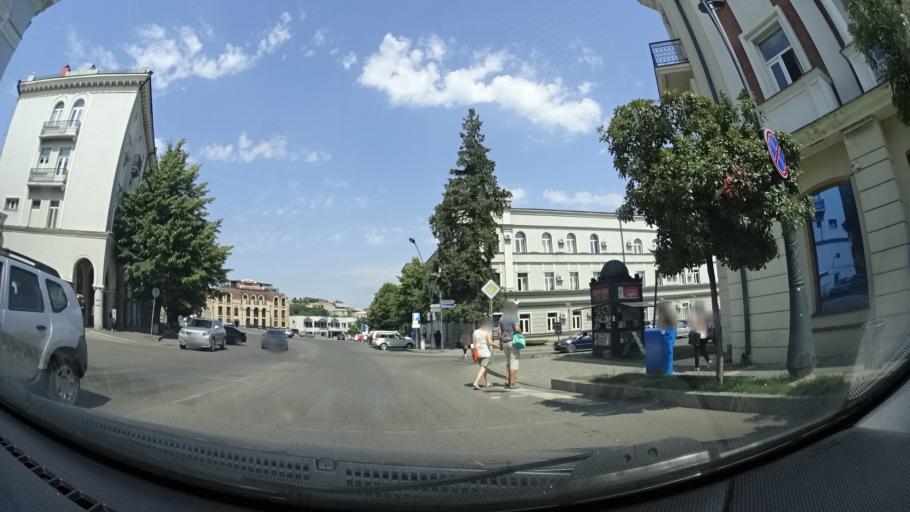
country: GE
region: Kakheti
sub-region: Telavi
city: Telavi
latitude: 41.9194
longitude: 45.4714
